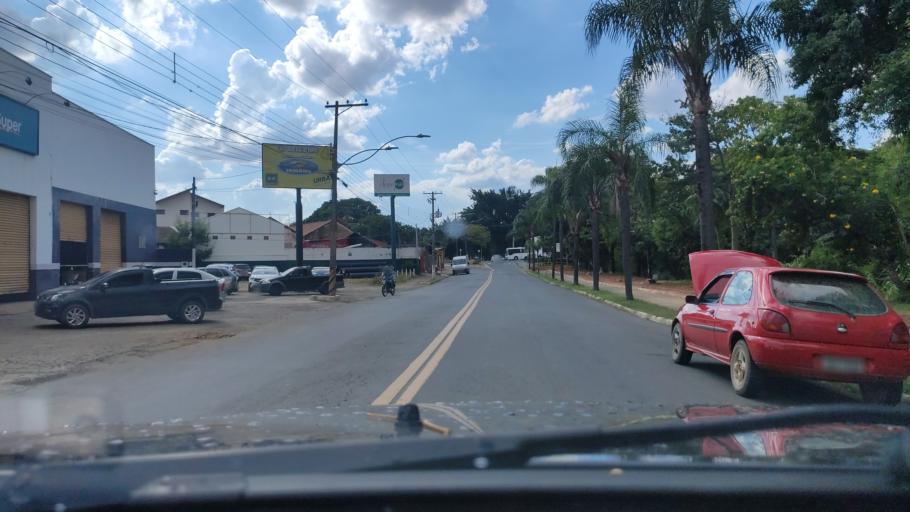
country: BR
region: Sao Paulo
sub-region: Itapira
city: Itapira
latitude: -22.4311
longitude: -46.8217
